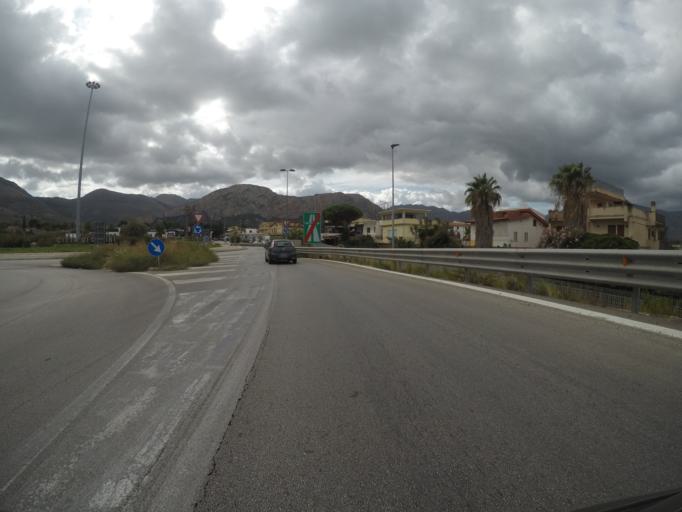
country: IT
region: Sicily
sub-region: Palermo
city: Capaci
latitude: 38.1735
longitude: 13.2150
